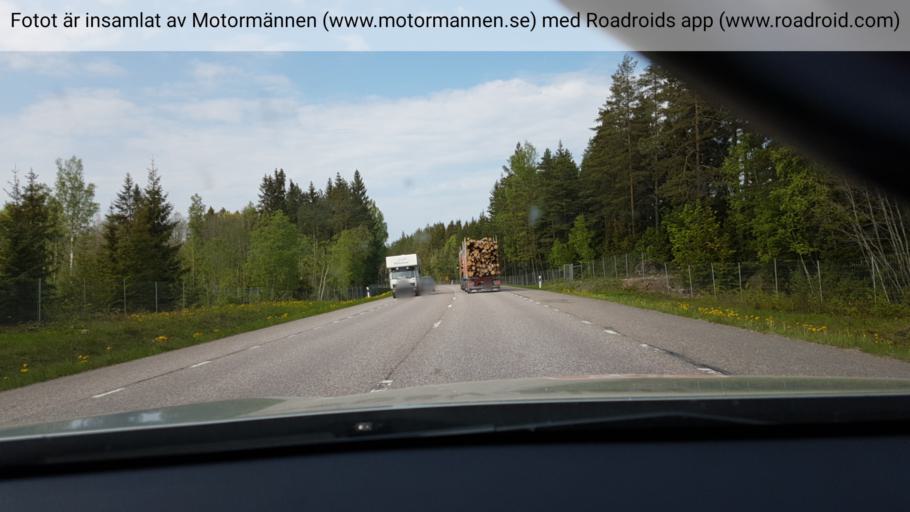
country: SE
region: Uppsala
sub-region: Alvkarleby Kommun
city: AElvkarleby
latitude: 60.5957
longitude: 17.4618
